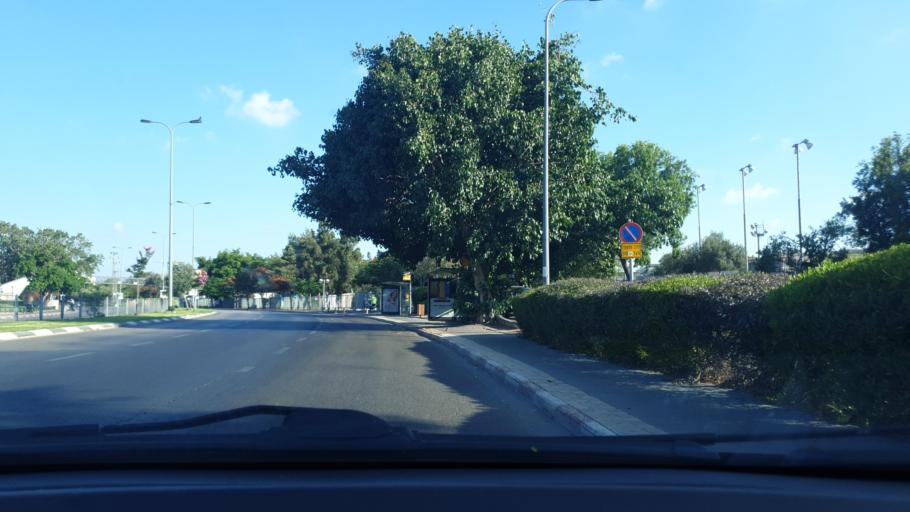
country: IL
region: Tel Aviv
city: Giv`atayim
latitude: 32.0589
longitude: 34.8039
